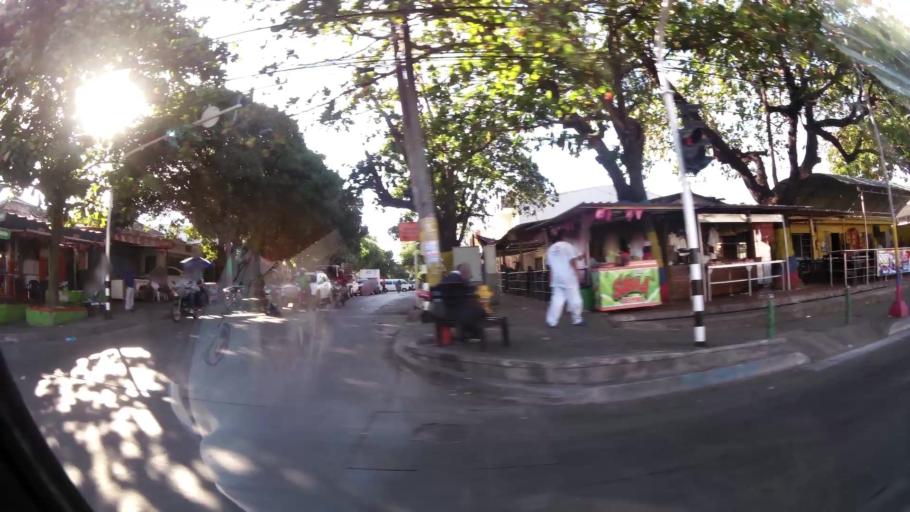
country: CO
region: Atlantico
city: Barranquilla
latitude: 10.9585
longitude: -74.7949
